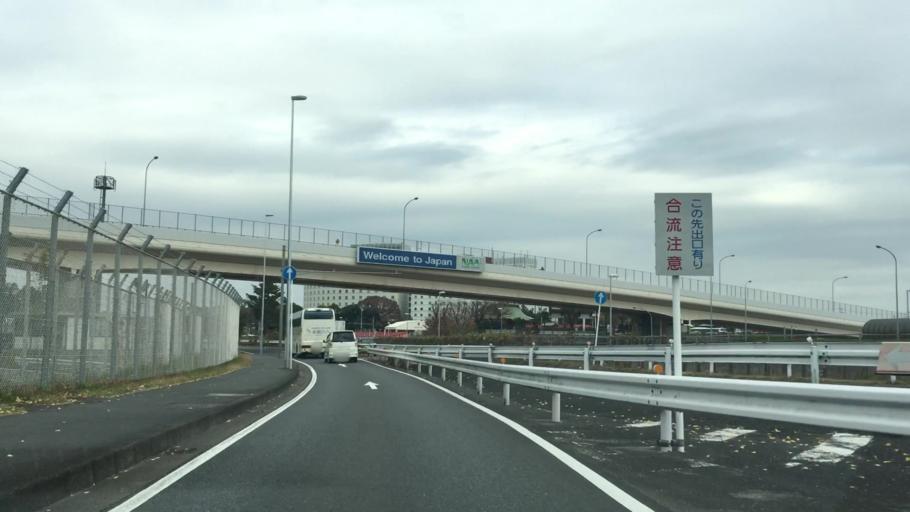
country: JP
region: Chiba
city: Narita
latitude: 35.7762
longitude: 140.3814
